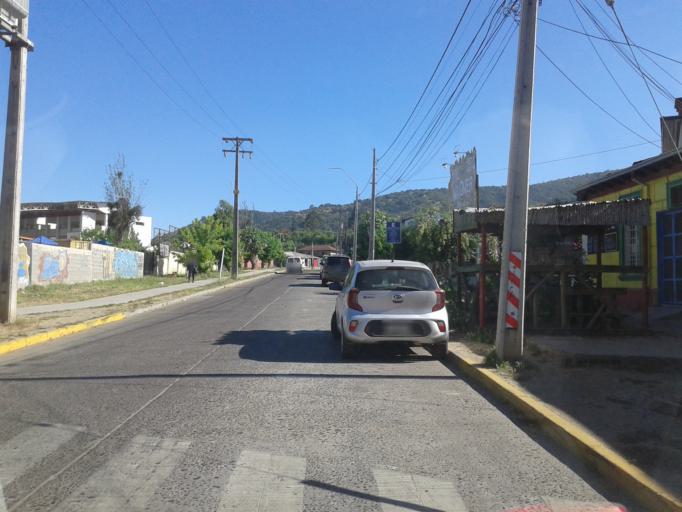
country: CL
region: Valparaiso
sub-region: Provincia de Marga Marga
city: Limache
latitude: -32.9866
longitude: -71.2723
